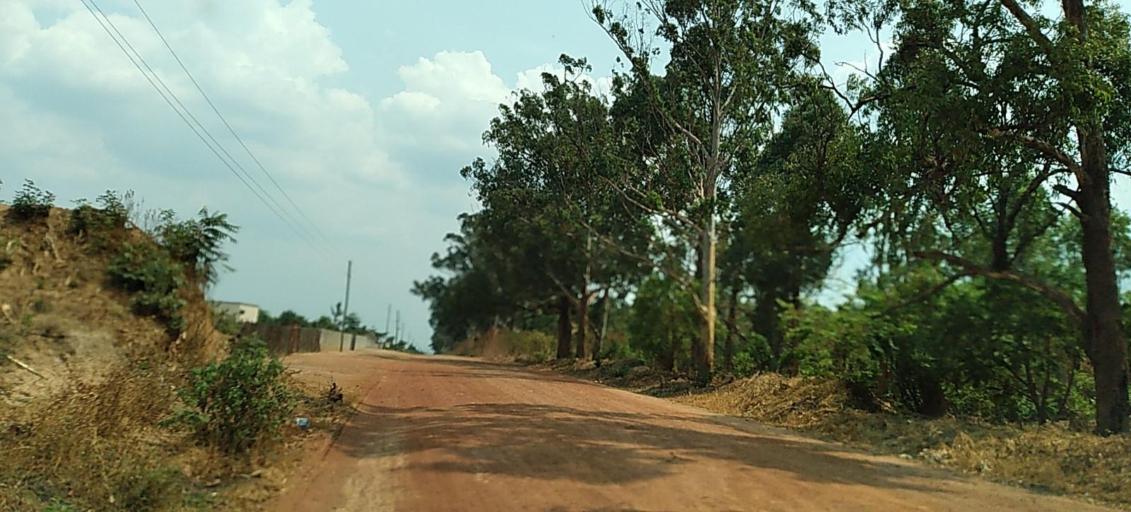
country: ZM
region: Copperbelt
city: Kalulushi
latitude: -12.8431
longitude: 28.0778
